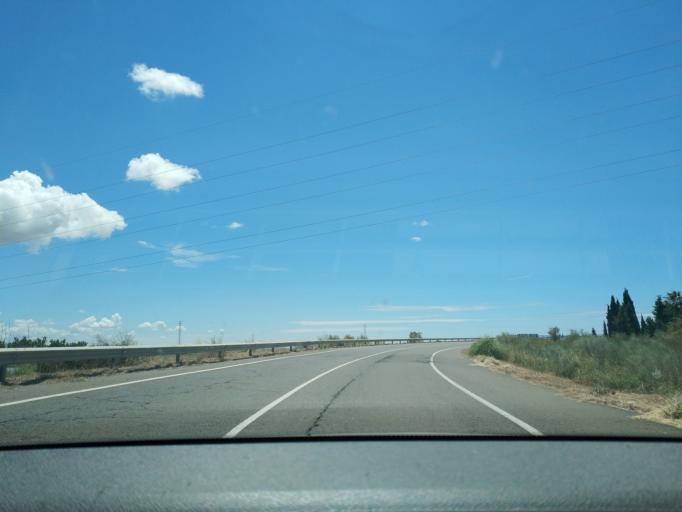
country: ES
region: Andalusia
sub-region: Provincia de Huelva
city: Aljaraque
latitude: 37.3246
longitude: -7.0723
